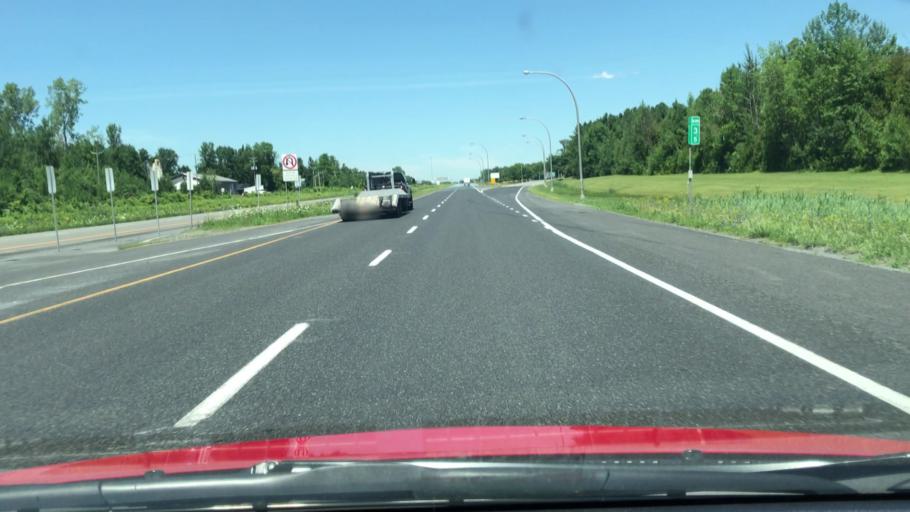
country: US
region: New York
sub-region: Clinton County
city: Champlain
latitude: 45.0435
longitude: -73.4536
